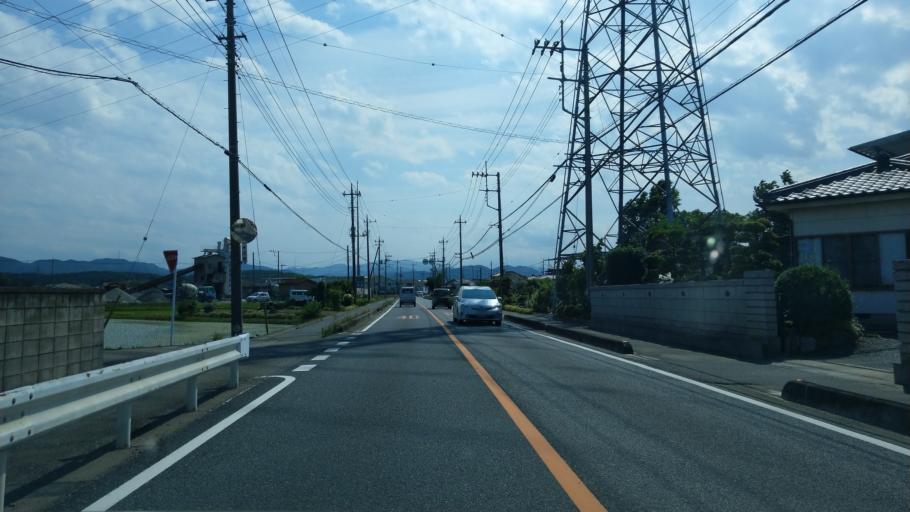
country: JP
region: Saitama
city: Kodamacho-kodamaminami
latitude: 36.2143
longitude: 139.1579
